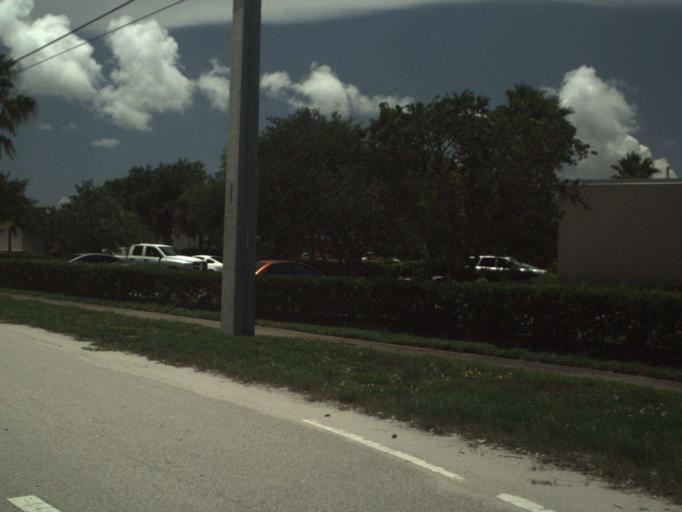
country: US
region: Florida
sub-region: Indian River County
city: Roseland
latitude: 27.8405
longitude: -80.4868
